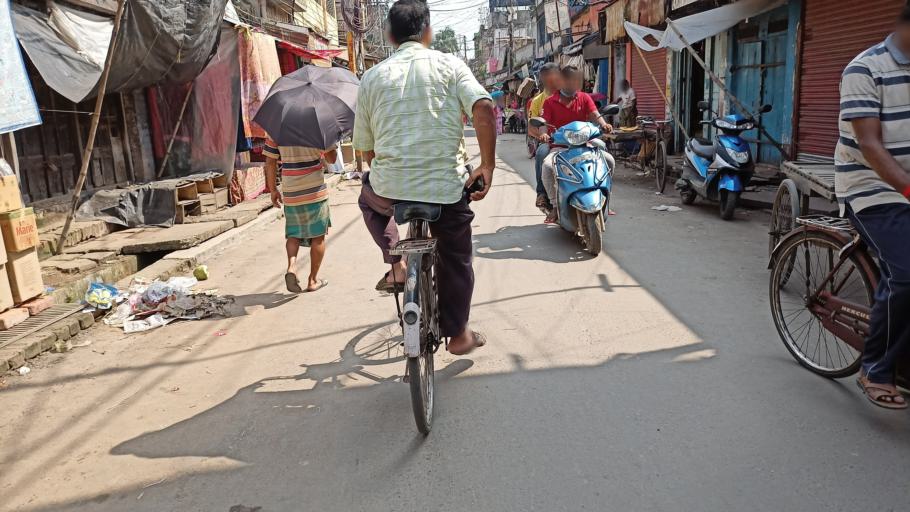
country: IN
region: West Bengal
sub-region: North 24 Parganas
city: Bangaon
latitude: 23.0454
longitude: 88.8308
